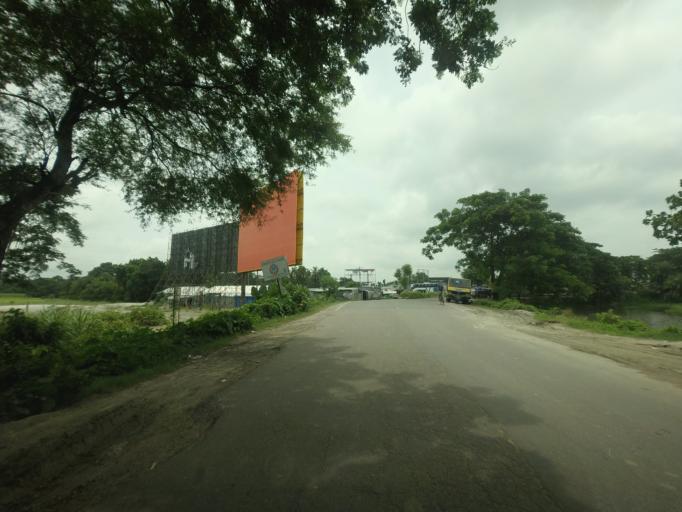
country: BD
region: Khulna
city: Kalia
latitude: 23.2127
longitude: 89.7096
